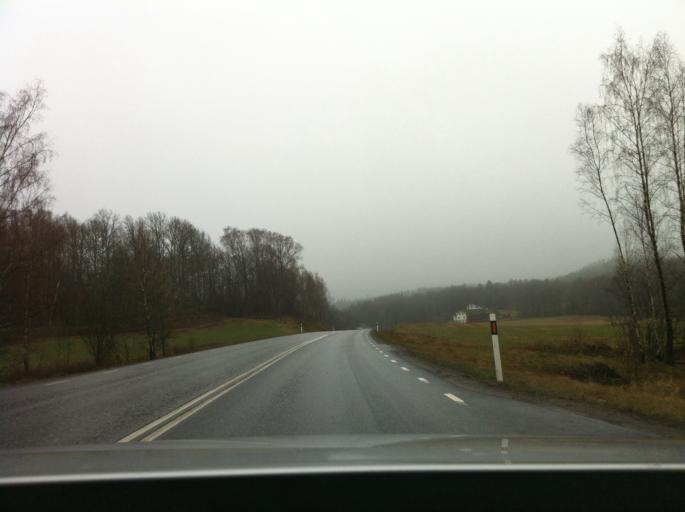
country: SE
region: Vaestra Goetaland
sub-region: Alingsas Kommun
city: Sollebrunn
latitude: 58.0480
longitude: 12.4684
